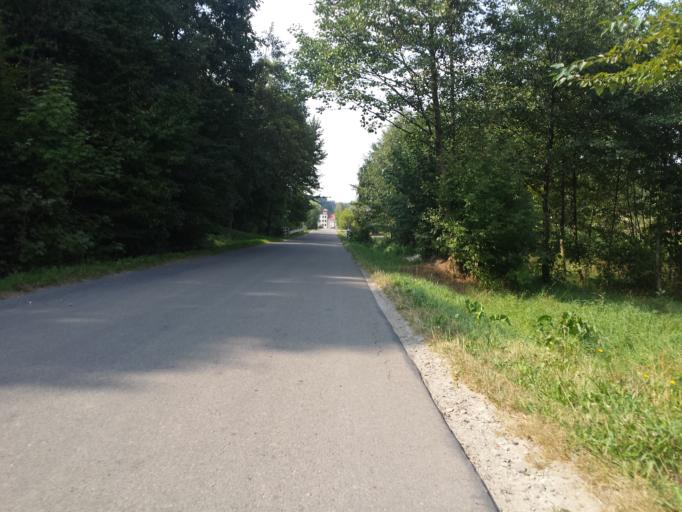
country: PL
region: Subcarpathian Voivodeship
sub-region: Powiat rzeszowski
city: Blazowa
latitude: 49.8524
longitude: 22.1376
